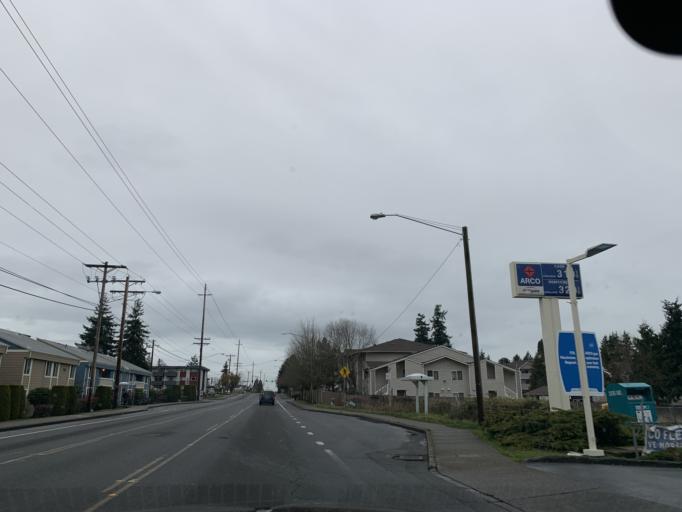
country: US
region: Washington
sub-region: Snohomish County
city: Mukilteo
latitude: 47.9219
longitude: -122.2463
